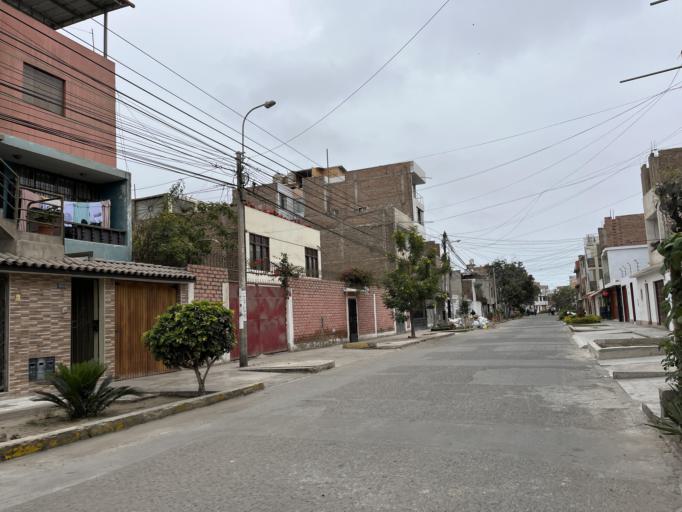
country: PE
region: La Libertad
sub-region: Provincia de Trujillo
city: Trujillo
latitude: -8.1284
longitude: -79.0196
